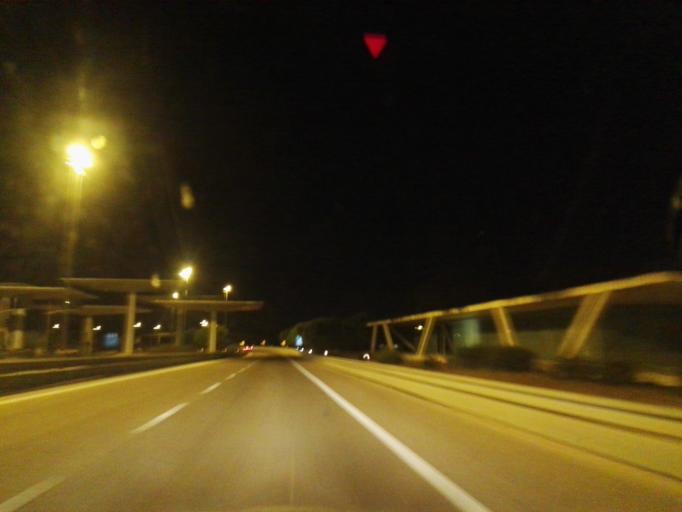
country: PT
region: Santarem
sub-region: Benavente
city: Benavente
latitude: 38.9579
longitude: -8.8296
